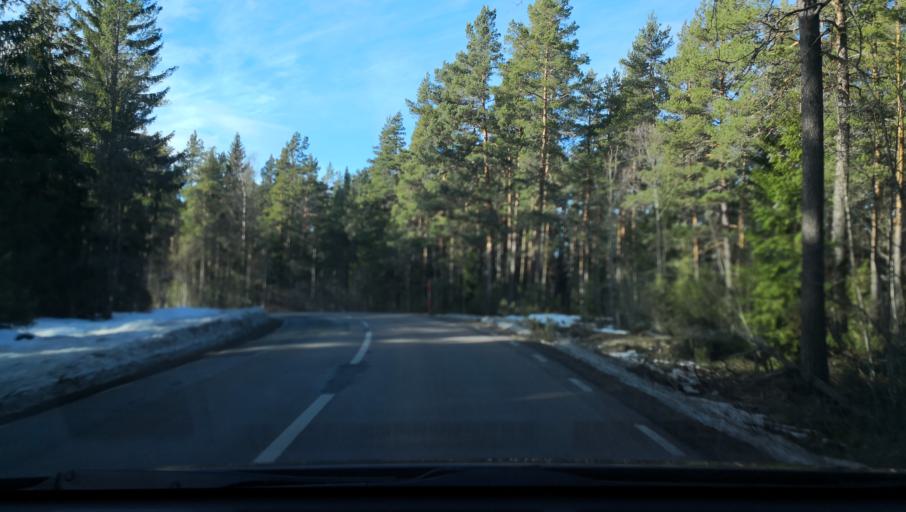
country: SE
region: Uppsala
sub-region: Osthammars Kommun
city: Osterbybruk
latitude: 60.2928
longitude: 18.0205
